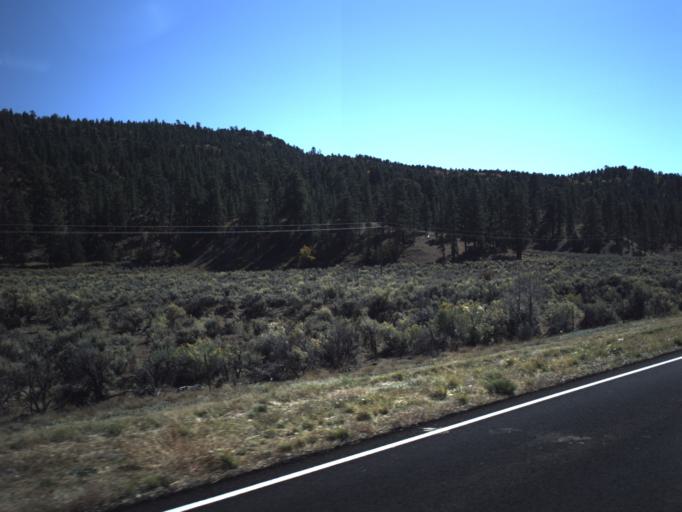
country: US
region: Utah
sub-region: Garfield County
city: Panguitch
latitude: 37.6605
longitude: -111.8341
